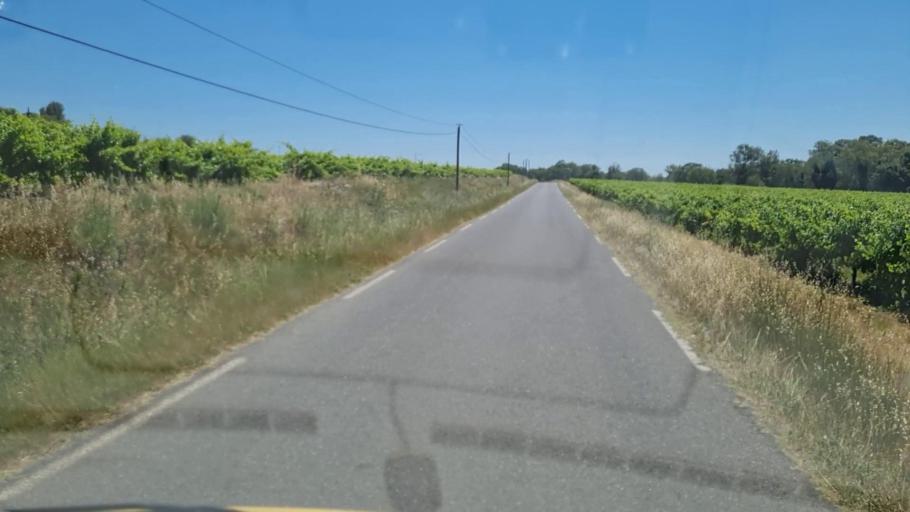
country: FR
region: Languedoc-Roussillon
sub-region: Departement du Gard
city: Le Cailar
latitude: 43.6527
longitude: 4.2533
